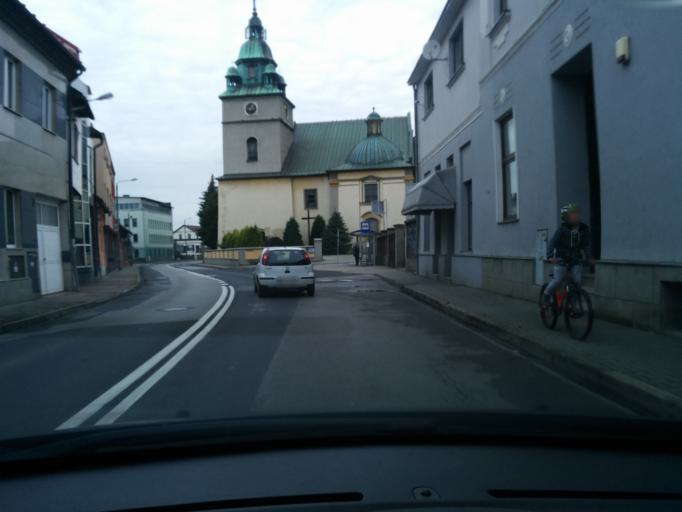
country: PL
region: Lesser Poland Voivodeship
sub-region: Powiat oswiecimski
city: Kety
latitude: 49.8838
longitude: 19.2207
